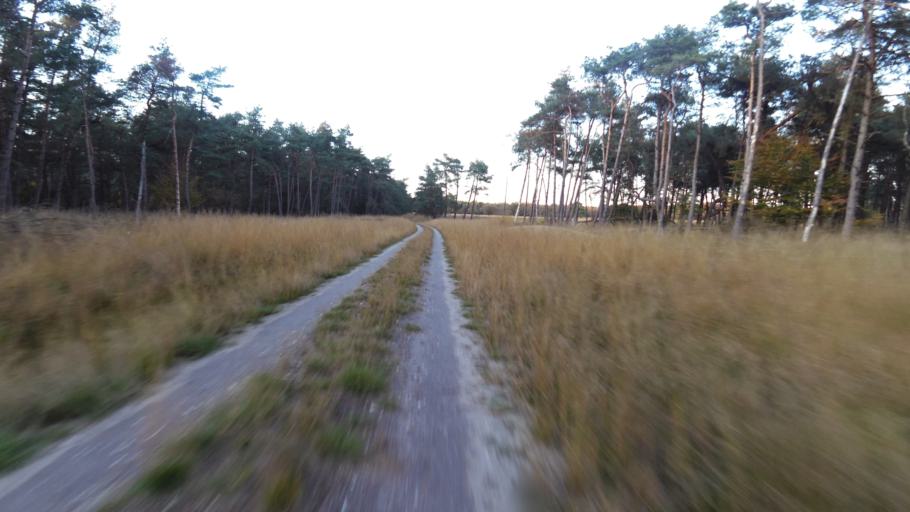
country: NL
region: Gelderland
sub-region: Gemeente Apeldoorn
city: Uddel
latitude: 52.2907
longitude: 5.8381
